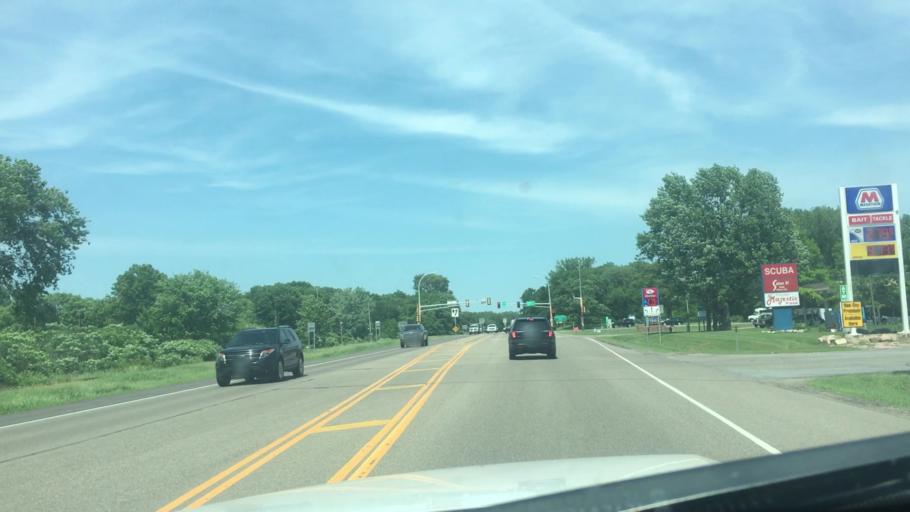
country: US
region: Minnesota
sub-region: Ramsey County
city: White Bear Lake
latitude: 45.1222
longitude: -93.0032
